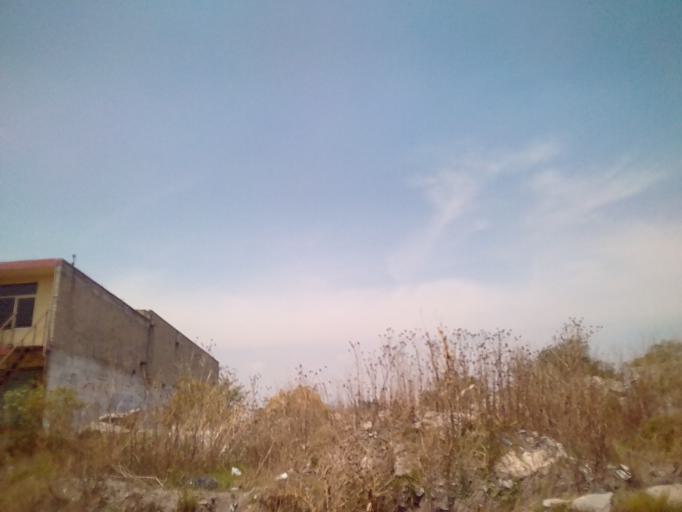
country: MX
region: Mexico
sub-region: Toluca
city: Guadalupe Totoltepec
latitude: 19.3489
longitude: -99.5578
